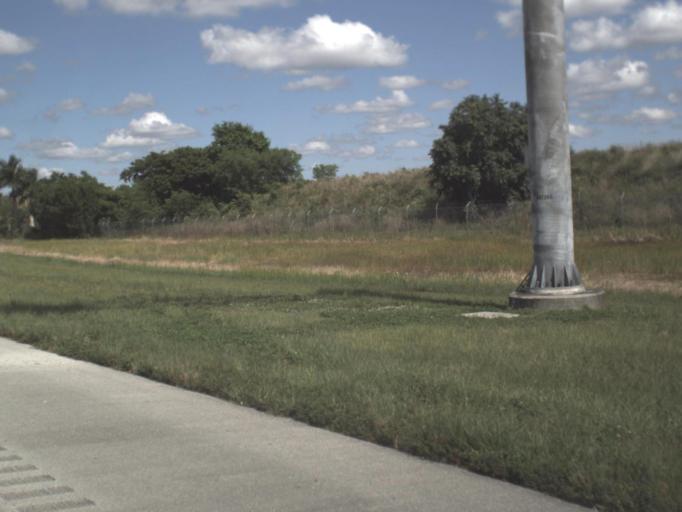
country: US
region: Florida
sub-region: Broward County
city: Coral Springs
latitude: 26.2950
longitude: -80.2969
